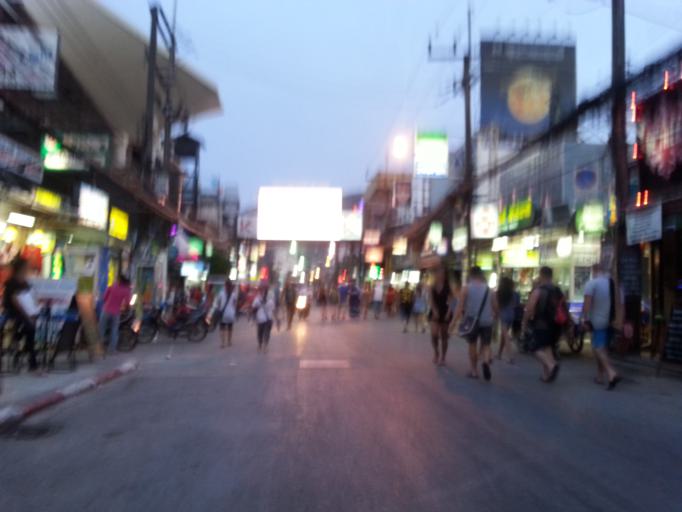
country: TH
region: Phuket
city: Patong
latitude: 7.8936
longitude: 98.2965
